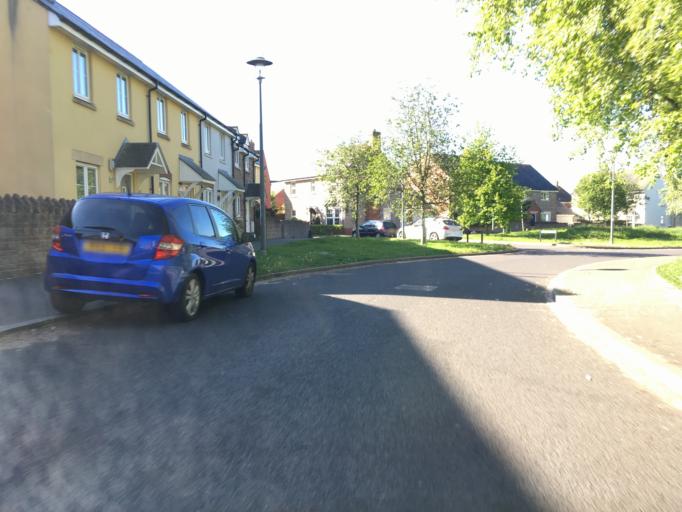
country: GB
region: England
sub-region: North Somerset
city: Portishead
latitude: 51.4872
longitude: -2.7500
